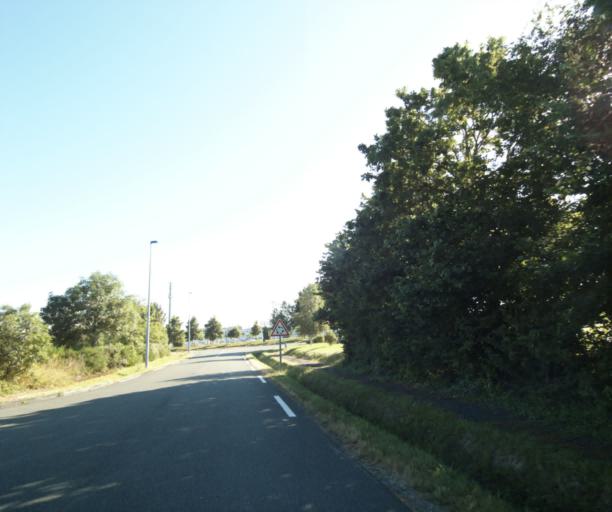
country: FR
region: Pays de la Loire
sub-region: Departement de la Mayenne
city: Laval
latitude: 48.0528
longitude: -0.7369
